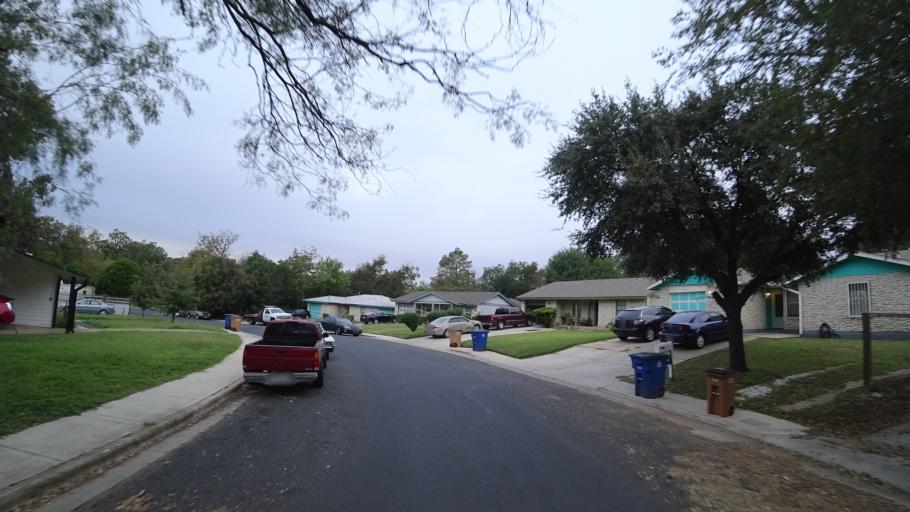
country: US
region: Texas
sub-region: Travis County
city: Austin
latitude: 30.2681
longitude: -97.7130
